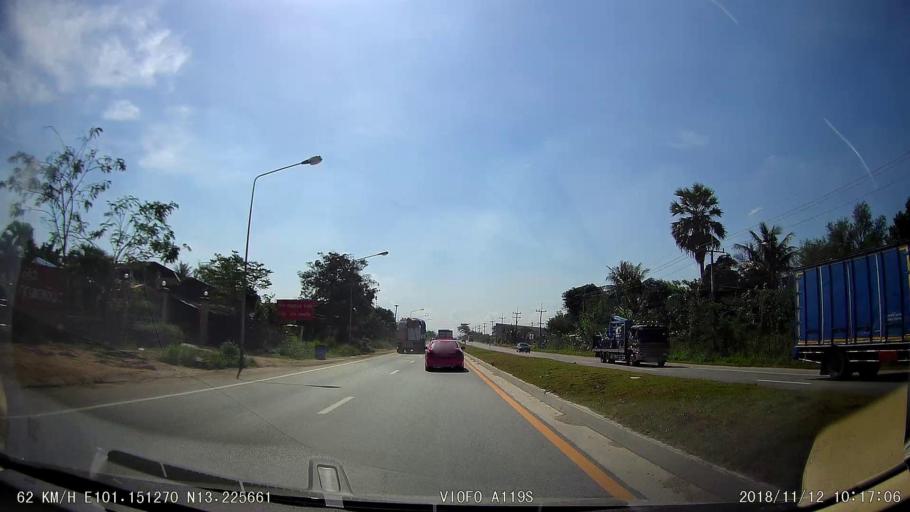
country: TH
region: Chon Buri
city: Ban Bueng
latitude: 13.2255
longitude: 101.1514
